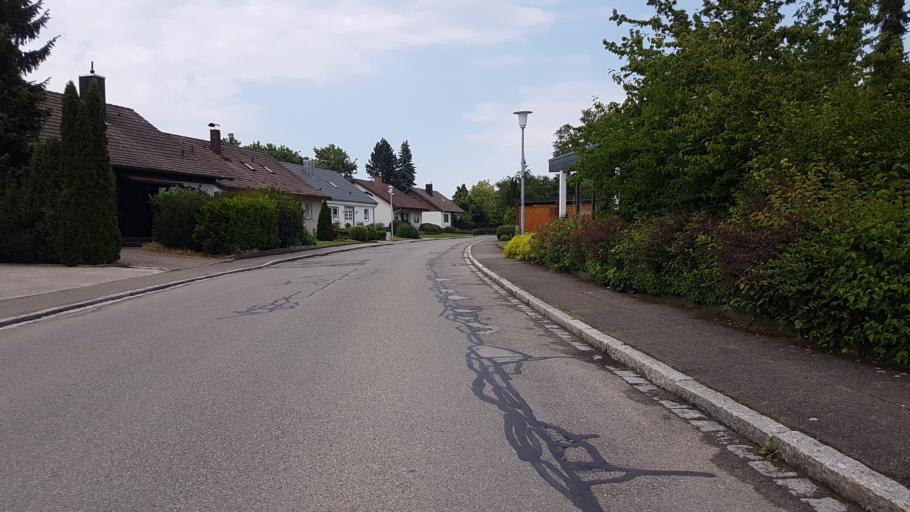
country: DE
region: Baden-Wuerttemberg
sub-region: Freiburg Region
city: Hufingen
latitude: 47.9225
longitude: 8.4980
